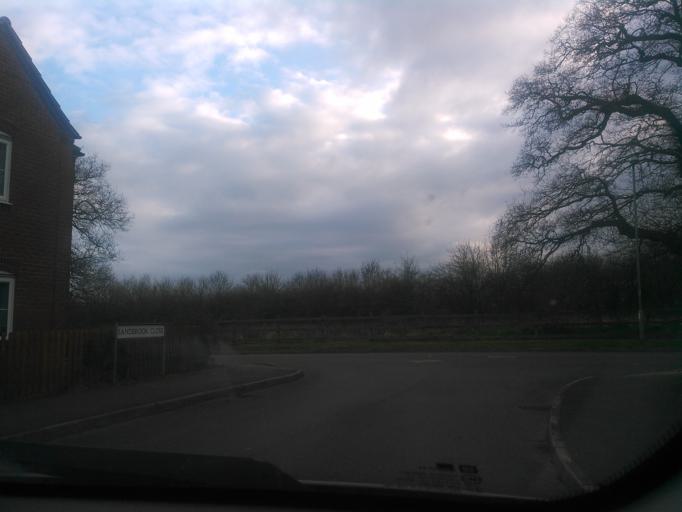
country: GB
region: England
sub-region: Shropshire
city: Stoke upon Tern
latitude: 52.8356
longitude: -2.4586
